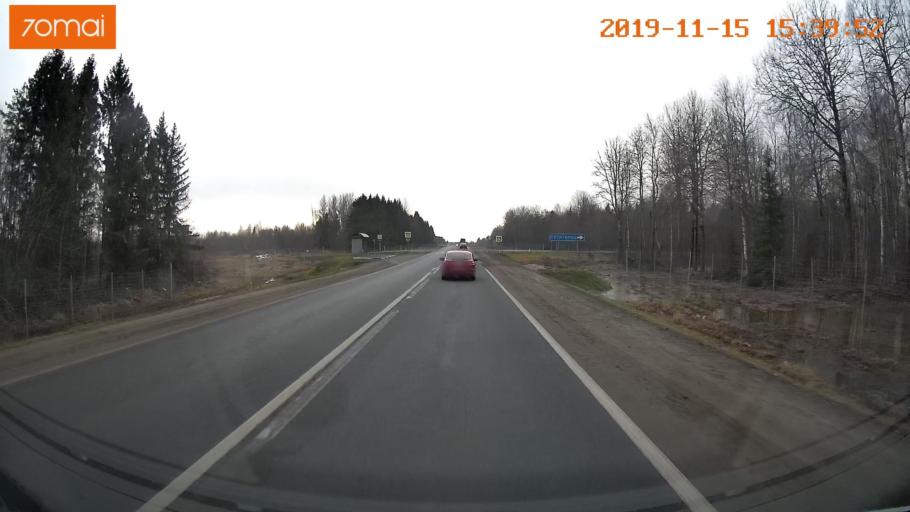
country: RU
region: Jaroslavl
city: Danilov
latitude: 58.0174
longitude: 40.0628
